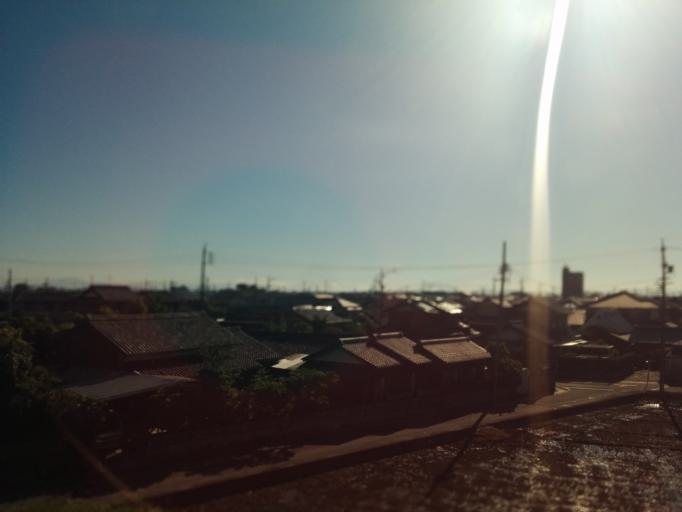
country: JP
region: Aichi
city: Inazawa
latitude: 35.2761
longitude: 136.7507
